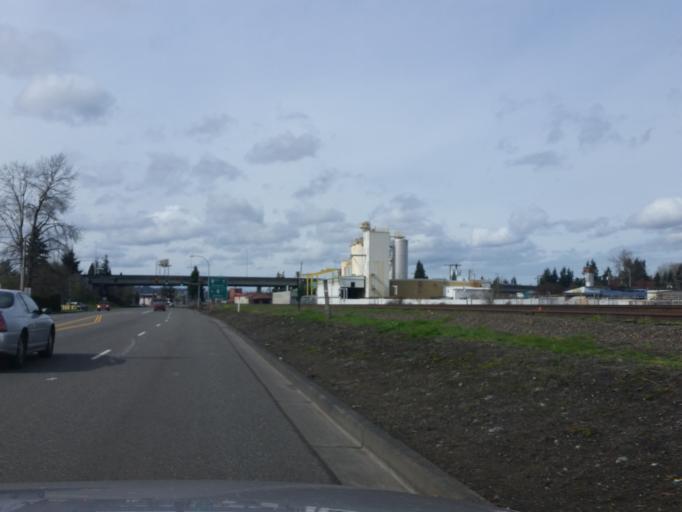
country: US
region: Washington
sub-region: Pierce County
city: Puyallup
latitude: 47.1896
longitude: -122.2789
